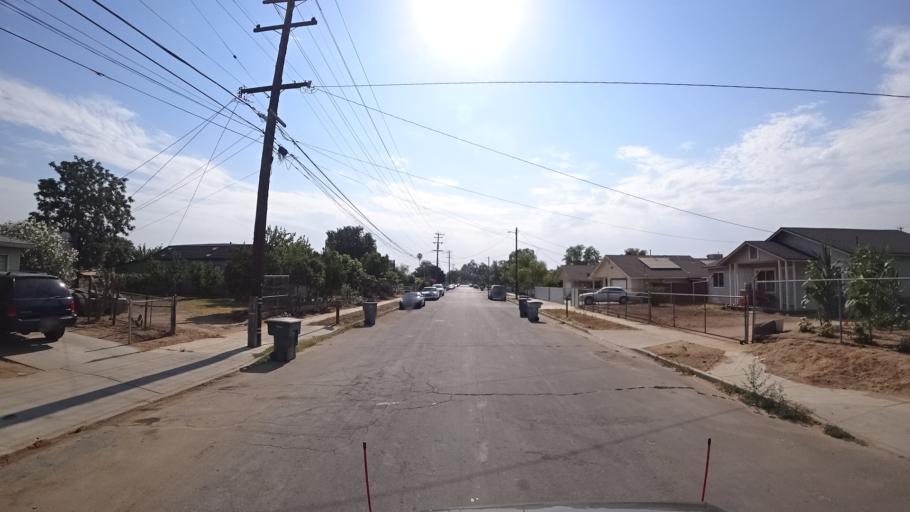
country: US
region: California
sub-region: Fresno County
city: West Park
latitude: 36.7187
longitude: -119.8152
